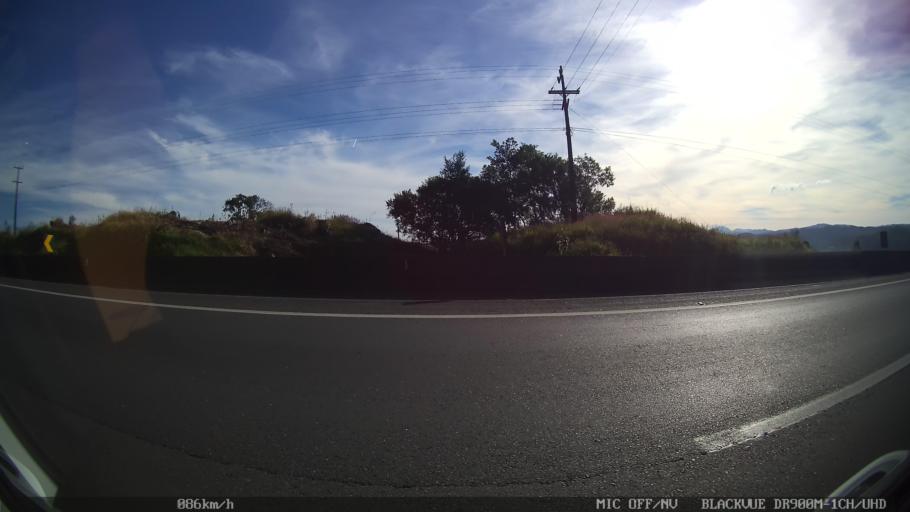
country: BR
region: Parana
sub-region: Campina Grande Do Sul
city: Campina Grande do Sul
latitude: -25.1550
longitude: -48.8608
